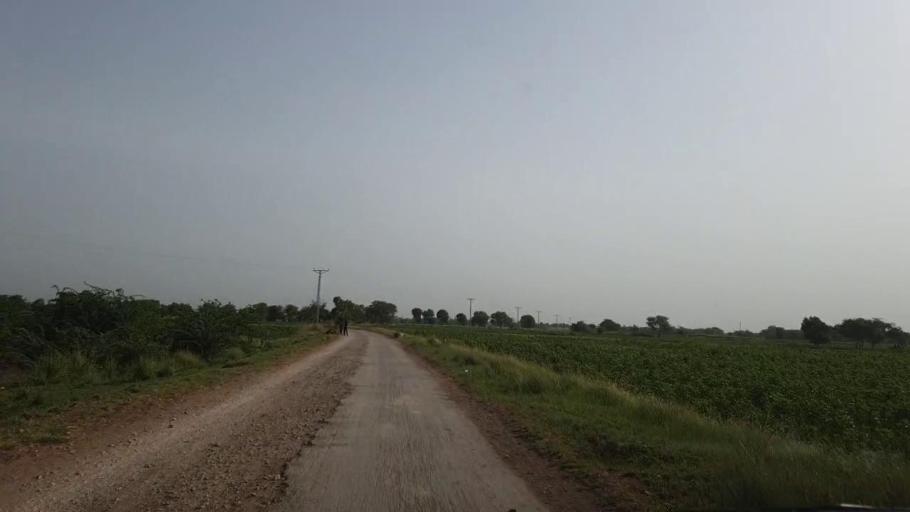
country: PK
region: Sindh
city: Nawabshah
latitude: 26.2200
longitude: 68.4045
